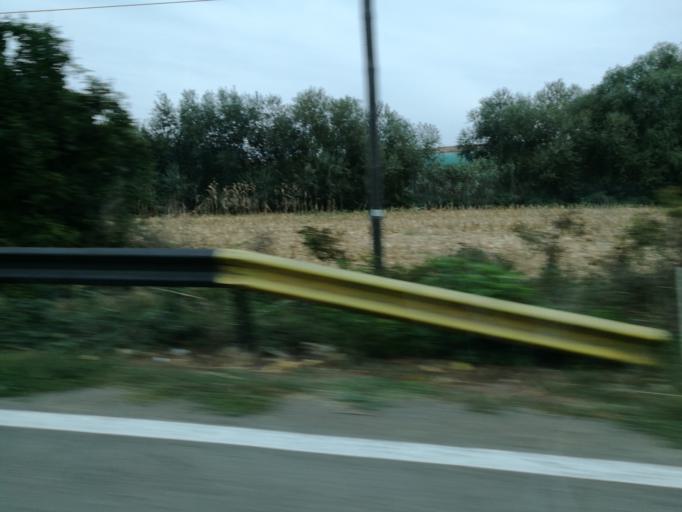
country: RO
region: Tulcea
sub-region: Comuna Ciucurova
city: Ciucurova
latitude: 44.9263
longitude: 28.4484
